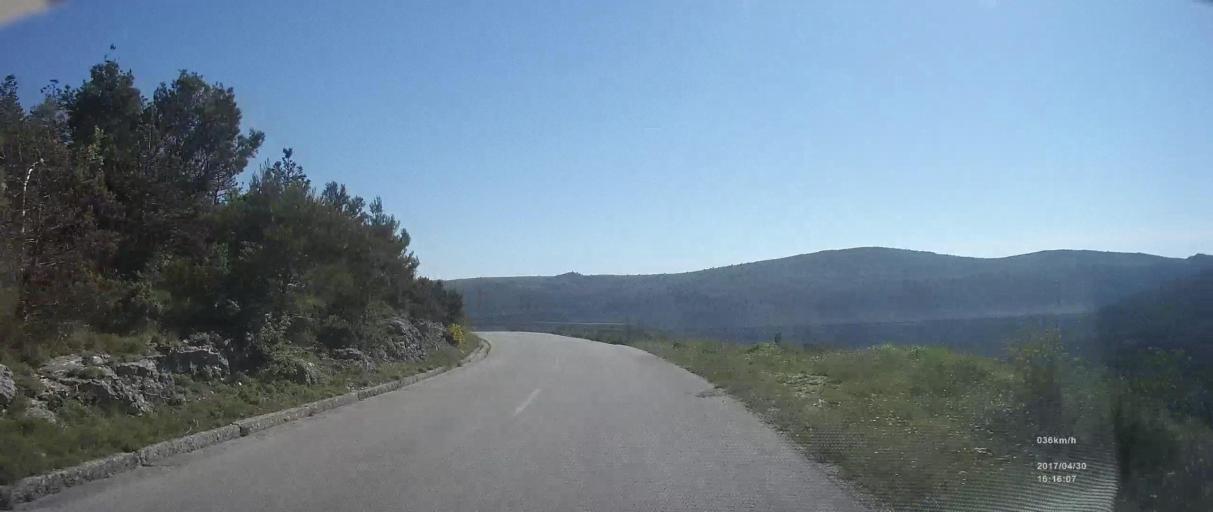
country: HR
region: Splitsko-Dalmatinska
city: Srinjine
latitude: 43.5045
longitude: 16.6058
